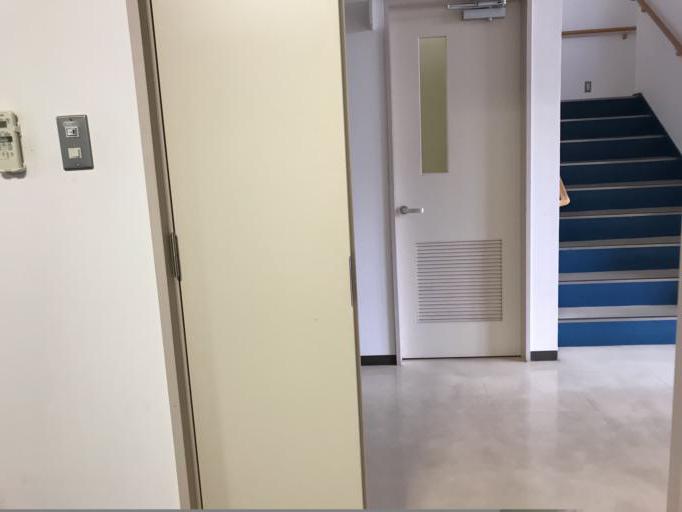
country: JP
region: Aichi
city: Obu
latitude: 35.0578
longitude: 136.9498
